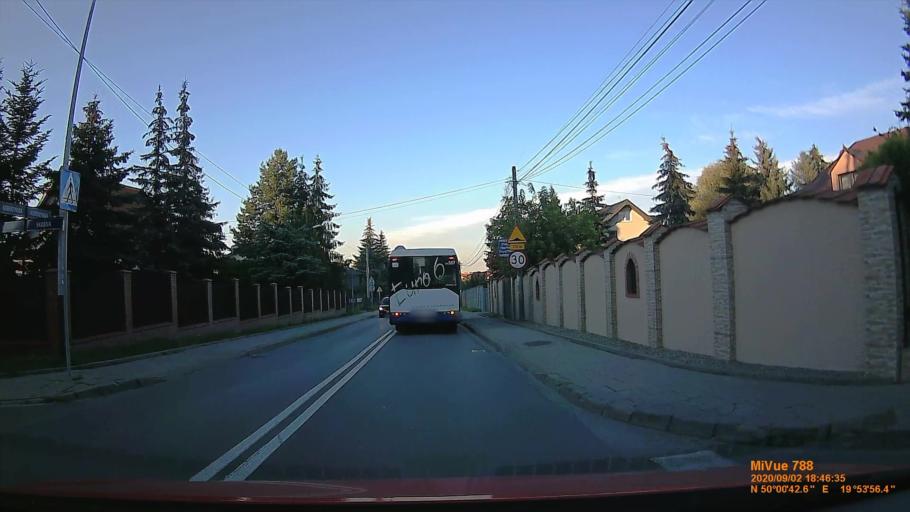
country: PL
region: Lesser Poland Voivodeship
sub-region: Krakow
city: Sidzina
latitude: 50.0120
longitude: 19.8992
